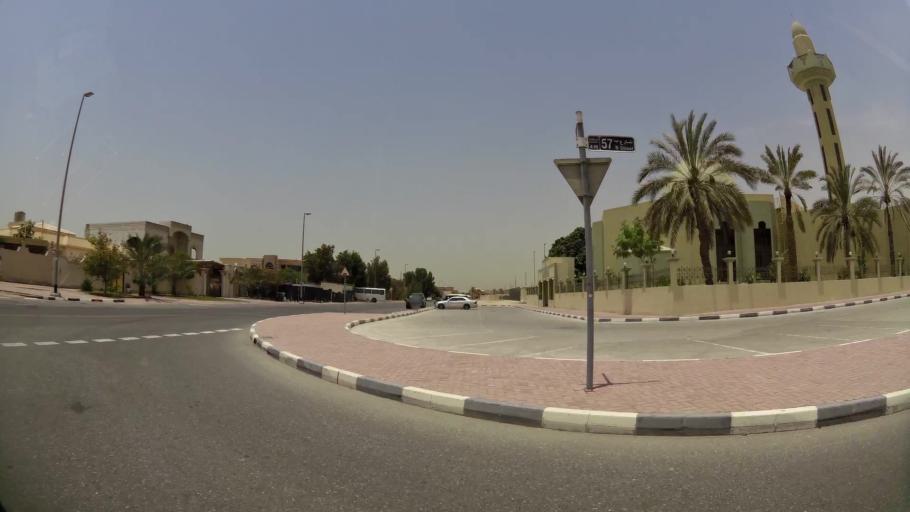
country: AE
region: Ash Shariqah
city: Sharjah
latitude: 25.2058
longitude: 55.3839
